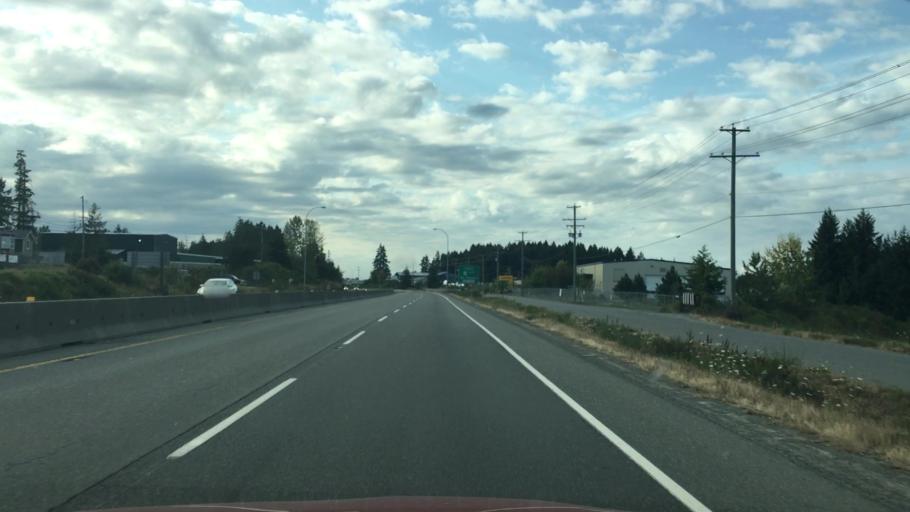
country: CA
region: British Columbia
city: Nanaimo
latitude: 49.1014
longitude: -123.8916
